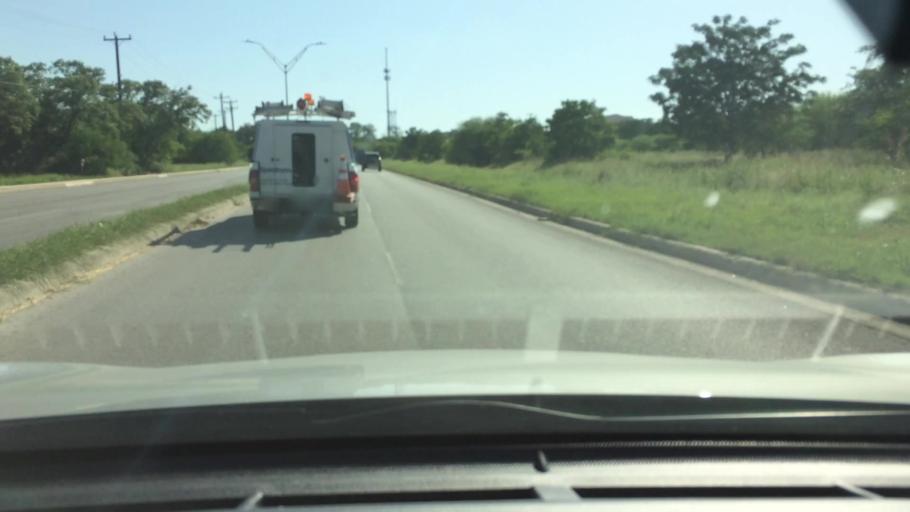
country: US
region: Texas
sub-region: Bexar County
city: Shavano Park
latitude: 29.5794
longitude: -98.5878
